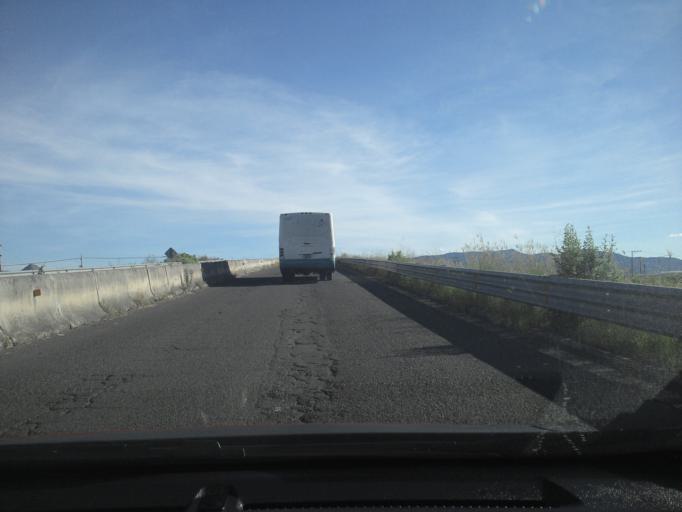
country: MX
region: Jalisco
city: El Refugio
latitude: 20.6588
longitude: -103.7336
